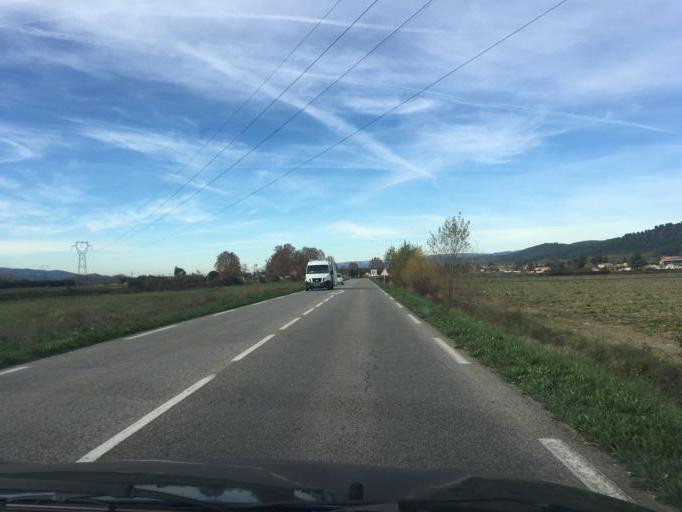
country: FR
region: Provence-Alpes-Cote d'Azur
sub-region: Departement du Vaucluse
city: Villelaure
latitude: 43.7052
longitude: 5.4357
